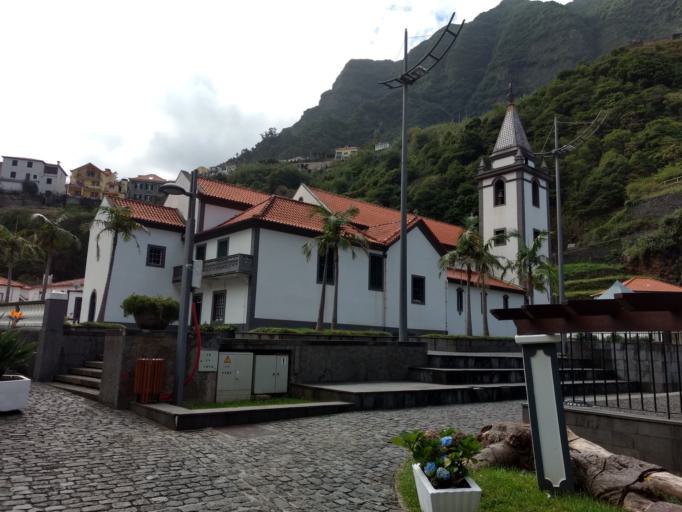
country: PT
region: Madeira
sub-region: Sao Vicente
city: Sao Vicente
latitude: 32.8041
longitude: -17.0468
